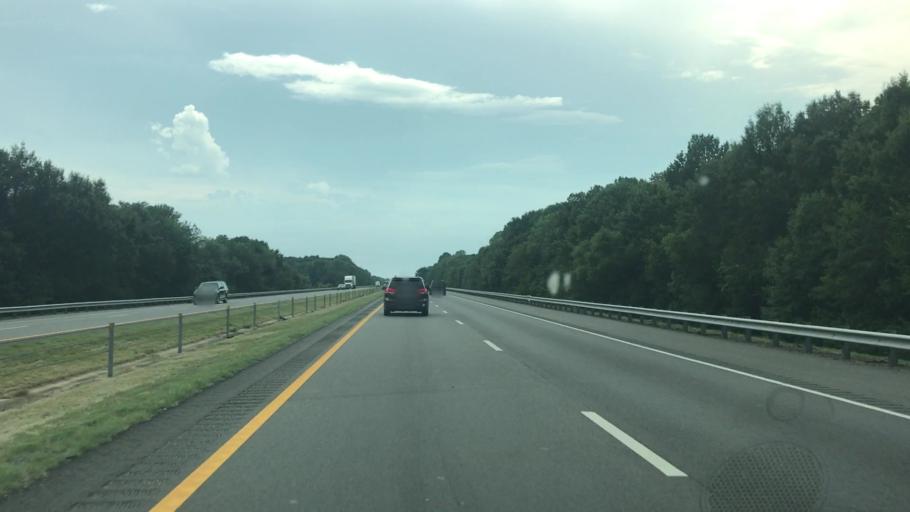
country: US
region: Arkansas
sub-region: Monroe County
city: Brinkley
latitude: 34.8924
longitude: -91.2500
